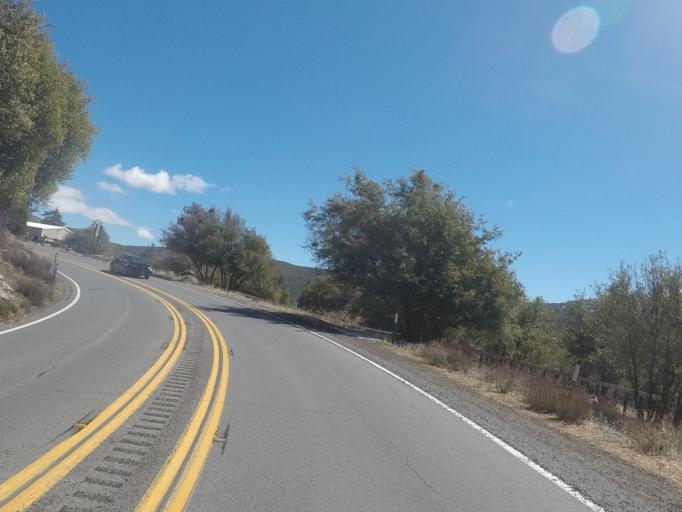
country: US
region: California
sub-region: Riverside County
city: Idyllwild
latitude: 33.7074
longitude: -116.7219
